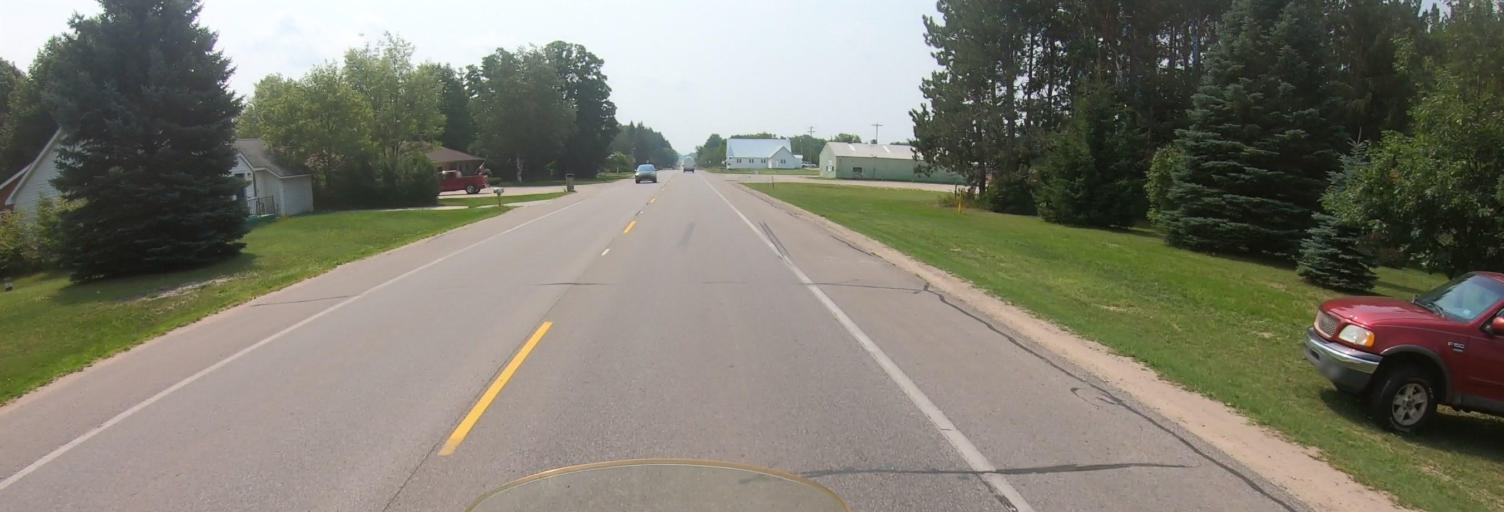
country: US
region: Michigan
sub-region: Luce County
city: Newberry
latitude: 46.3274
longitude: -85.5097
